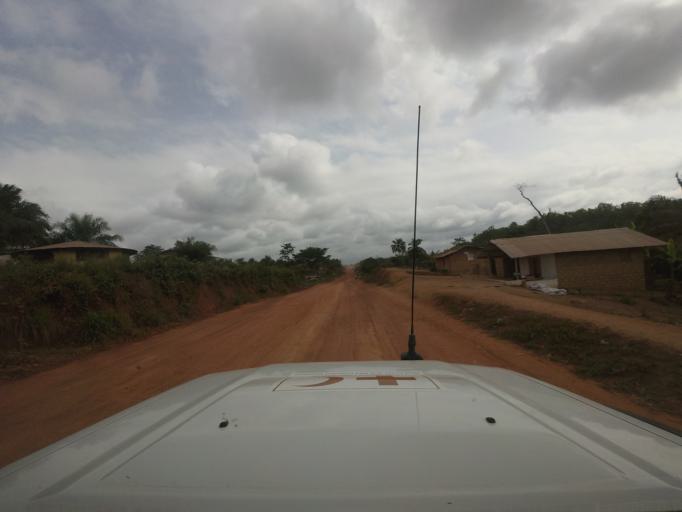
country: LR
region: Bong
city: Gbarnga
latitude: 7.0195
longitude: -9.4728
